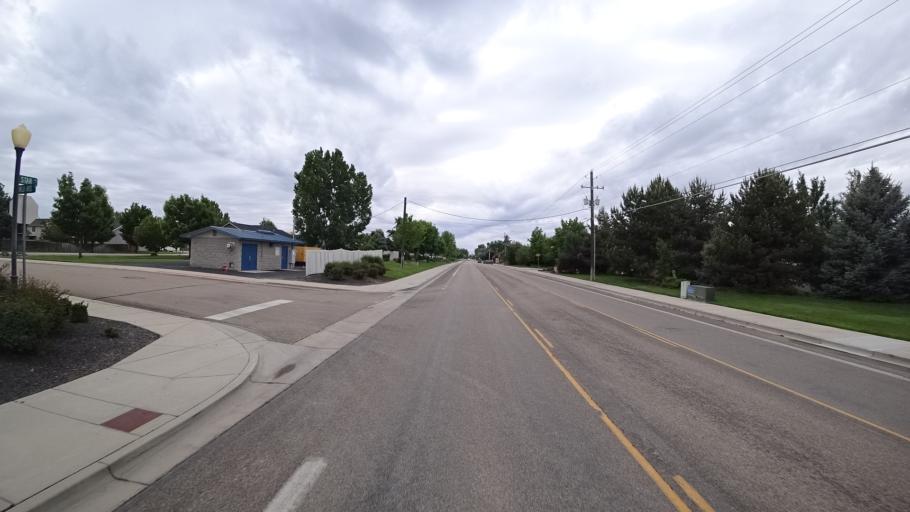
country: US
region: Idaho
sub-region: Ada County
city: Star
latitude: 43.7025
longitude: -116.4933
